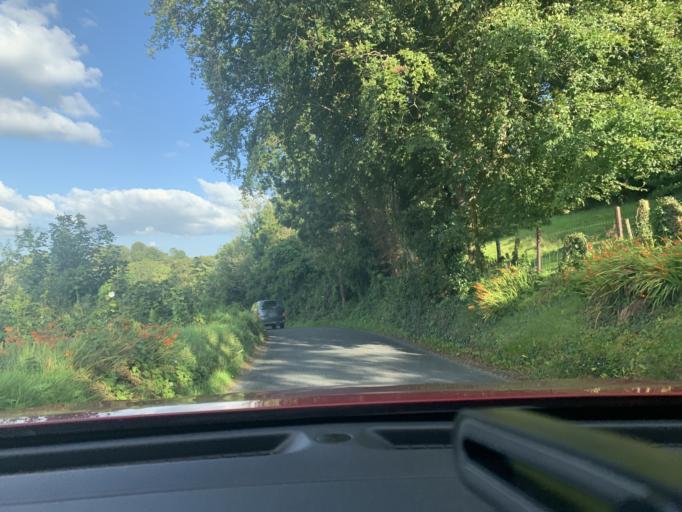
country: IE
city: Ballisodare
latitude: 54.2004
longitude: -8.5799
